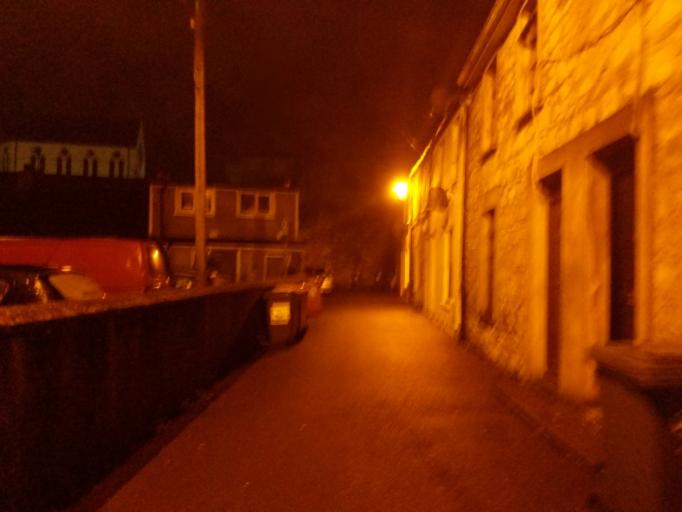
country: IE
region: Munster
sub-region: County Cork
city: Cork
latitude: 51.8948
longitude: -8.4640
